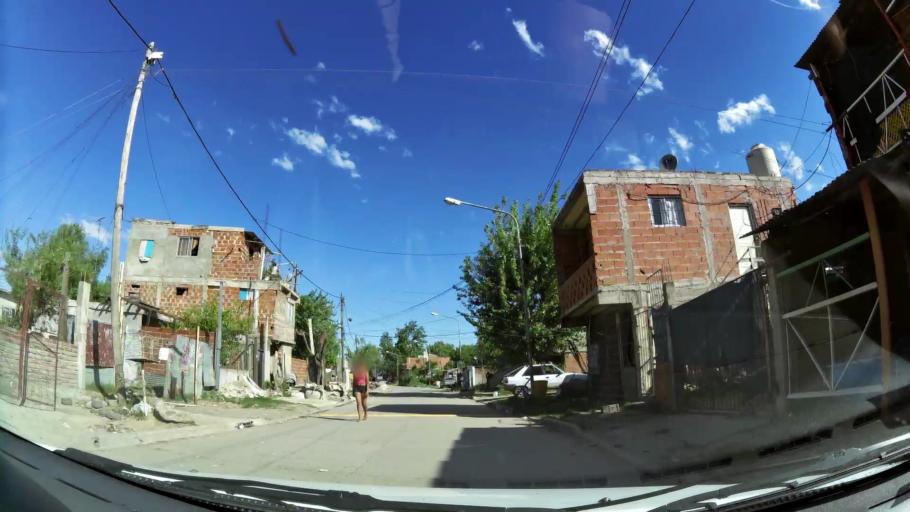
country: AR
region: Buenos Aires
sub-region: Partido de General San Martin
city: General San Martin
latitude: -34.5203
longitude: -58.5851
